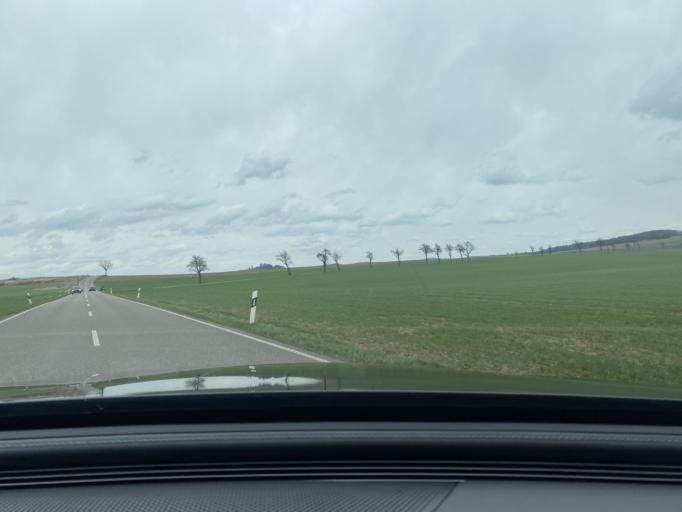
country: DE
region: Saxony
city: Durrrohrsdorf
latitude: 51.0255
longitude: 14.0348
